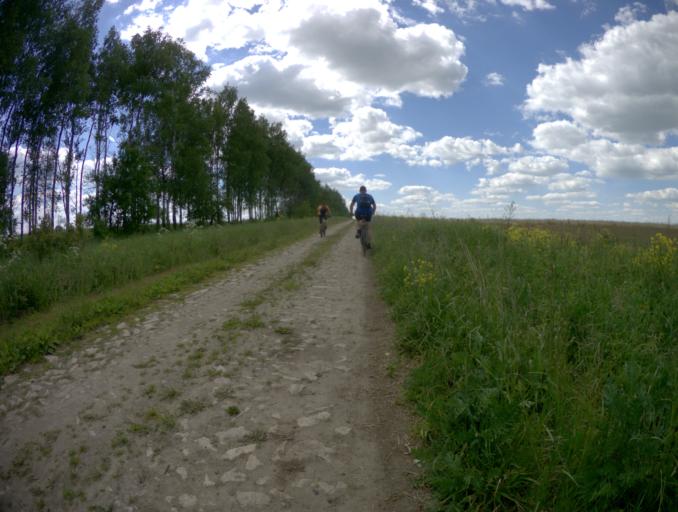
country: RU
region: Vladimir
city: Vladimir
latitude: 56.2704
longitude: 40.4103
